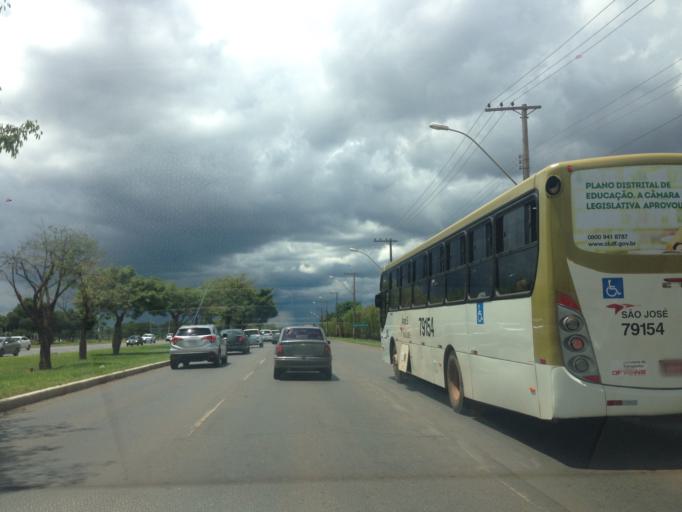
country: BR
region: Federal District
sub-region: Brasilia
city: Brasilia
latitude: -15.8248
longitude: -47.9338
